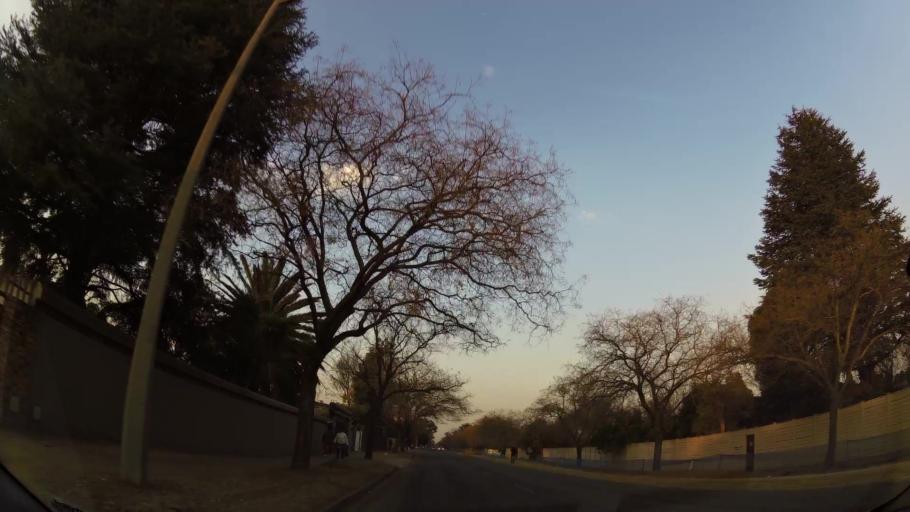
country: ZA
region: Gauteng
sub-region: Ekurhuleni Metropolitan Municipality
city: Benoni
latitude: -26.1732
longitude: 28.3371
